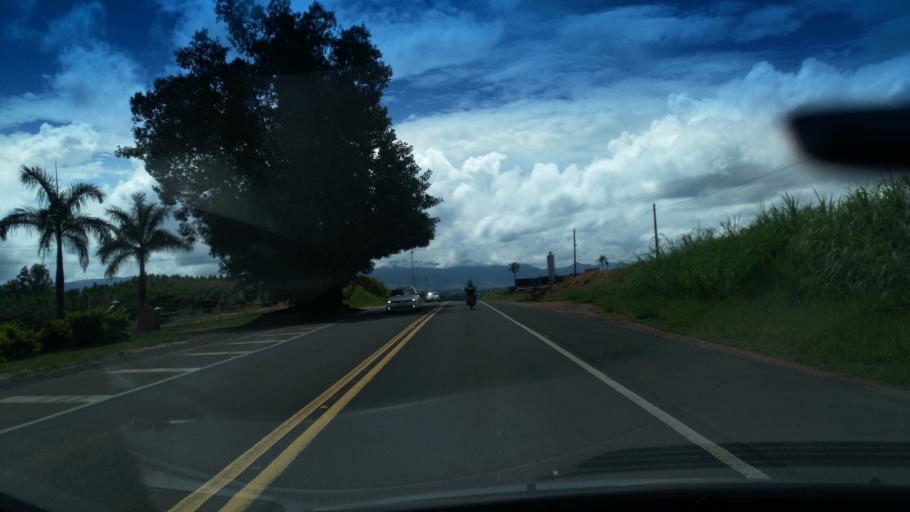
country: BR
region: Sao Paulo
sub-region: Santo Antonio Do Jardim
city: Espirito Santo do Pinhal
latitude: -22.1298
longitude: -46.6938
